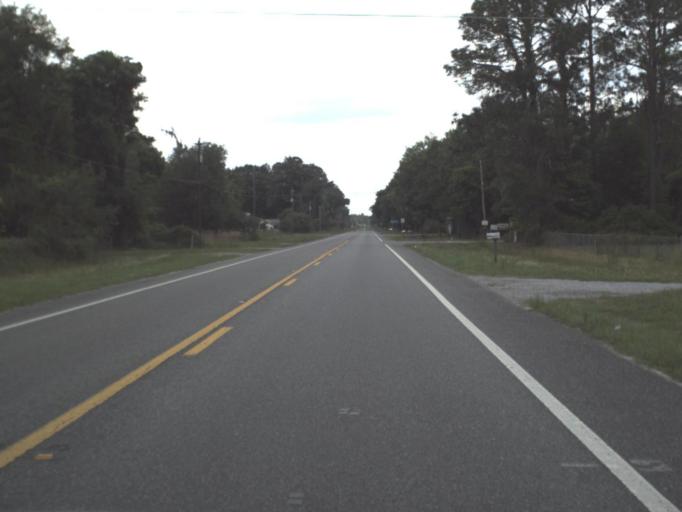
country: US
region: Florida
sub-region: Columbia County
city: Five Points
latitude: 30.2456
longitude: -82.6384
